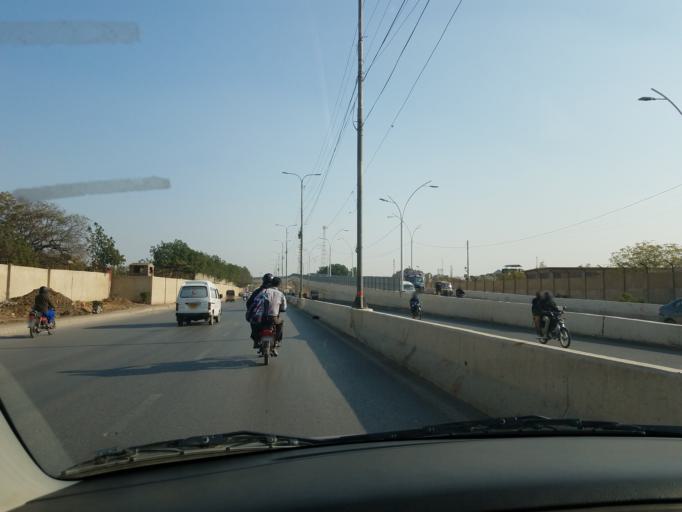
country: PK
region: Sindh
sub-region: Karachi District
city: Karachi
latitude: 24.8896
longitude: 67.1237
